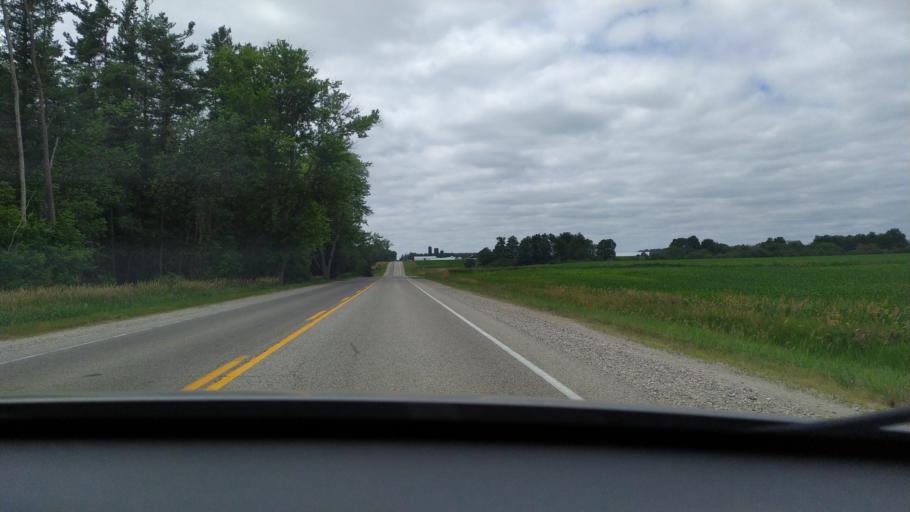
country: CA
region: Ontario
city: Stratford
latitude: 43.3237
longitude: -80.9559
